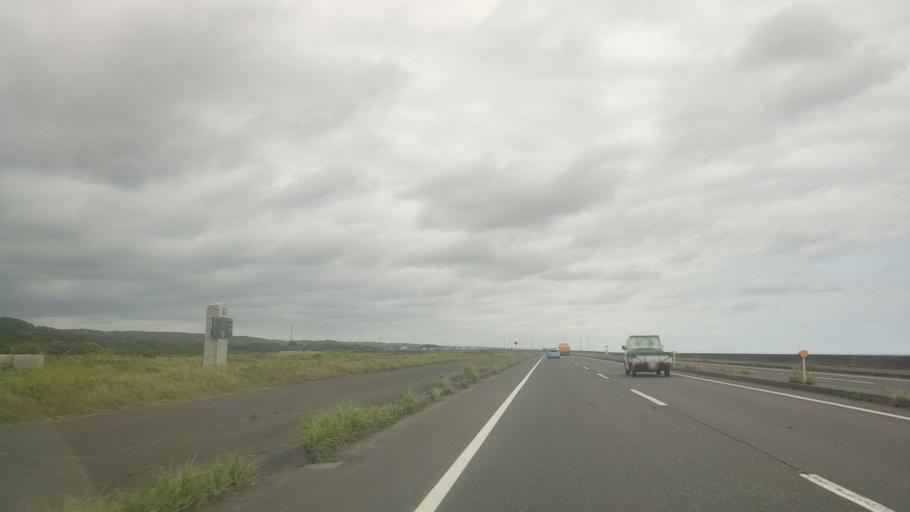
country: JP
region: Hokkaido
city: Shiraoi
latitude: 42.5555
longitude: 141.3752
